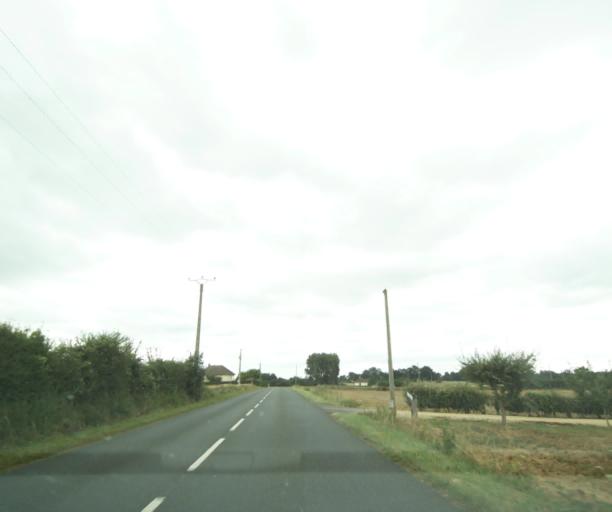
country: FR
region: Pays de la Loire
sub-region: Departement de la Sarthe
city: Precigne
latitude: 47.7807
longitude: -0.3173
